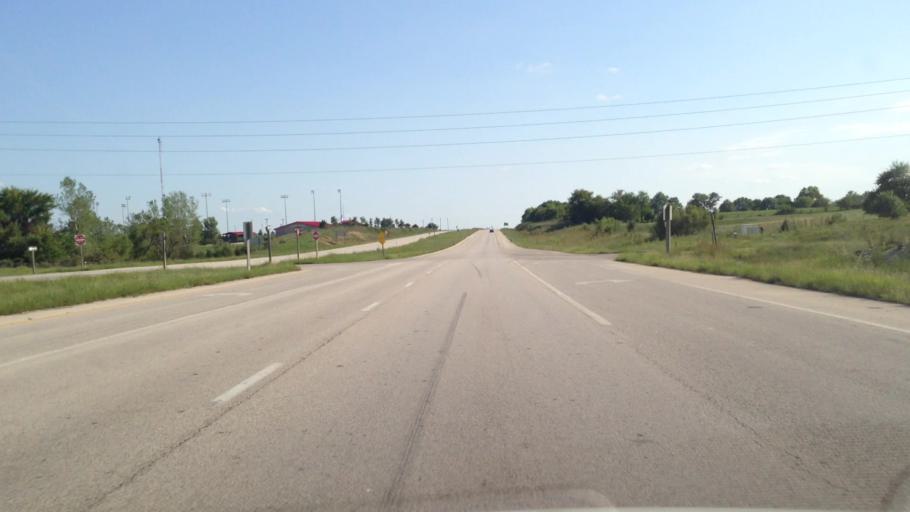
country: US
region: Kansas
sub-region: Bourbon County
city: Fort Scott
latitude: 37.7912
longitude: -94.7048
